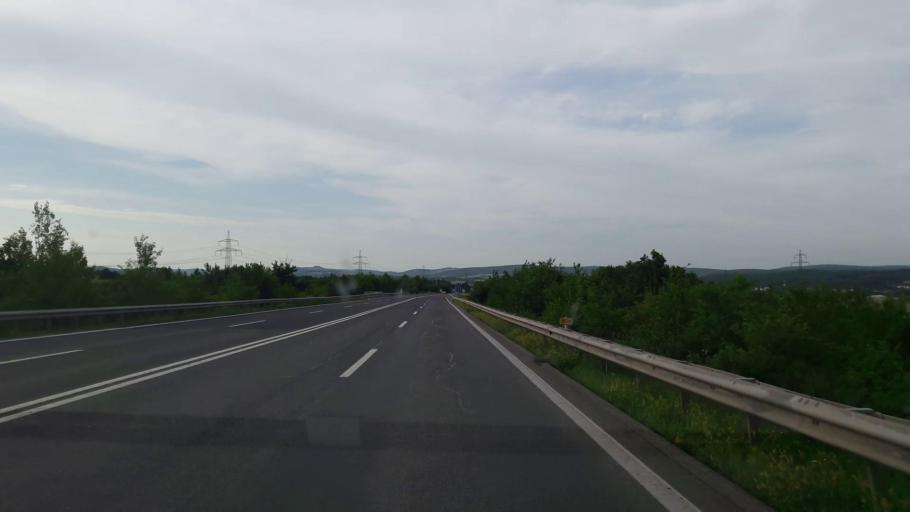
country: AT
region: Burgenland
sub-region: Politischer Bezirk Oberpullendorf
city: Markt Sankt Martin
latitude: 47.5605
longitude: 16.4166
